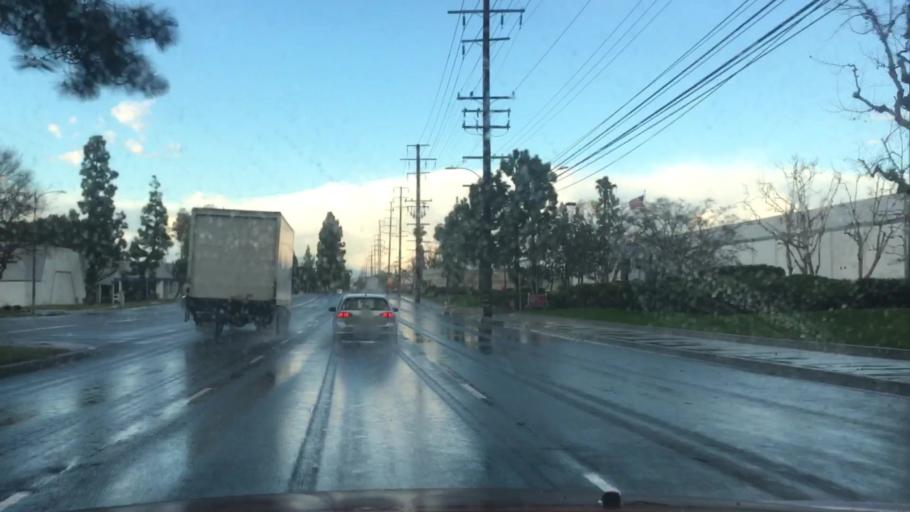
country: US
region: California
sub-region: Orange County
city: La Palma
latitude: 33.8689
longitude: -118.0287
